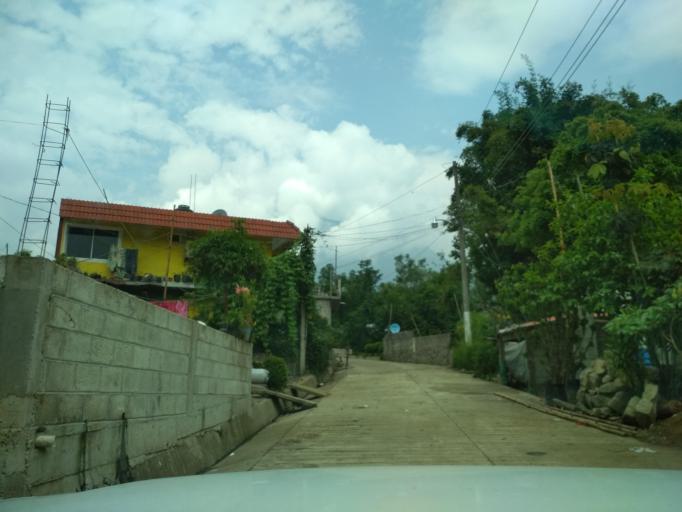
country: MX
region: Veracruz
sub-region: La Perla
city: La Perla
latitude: 18.9274
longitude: -97.1282
